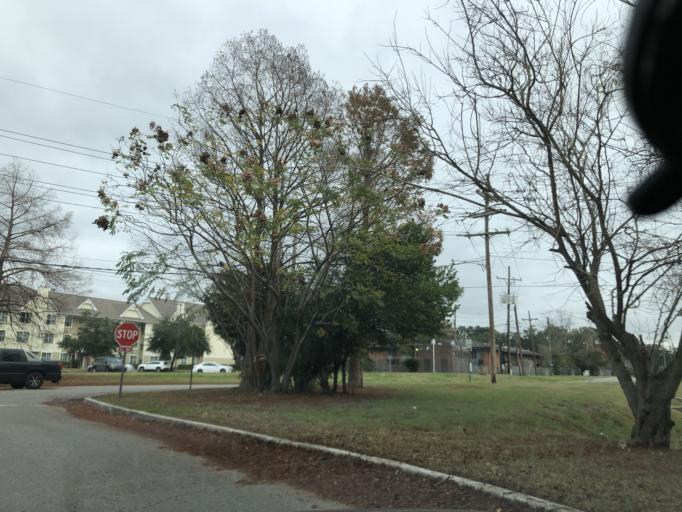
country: US
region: Louisiana
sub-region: Jefferson Parish
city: Metairie
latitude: 29.9921
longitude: -90.1529
